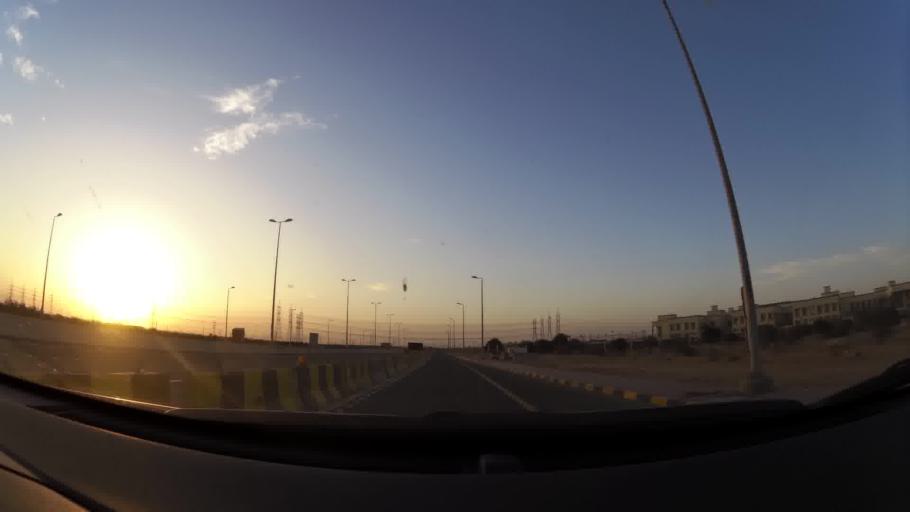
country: KW
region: Muhafazat al Jahra'
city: Al Jahra'
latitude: 29.3201
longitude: 47.7900
